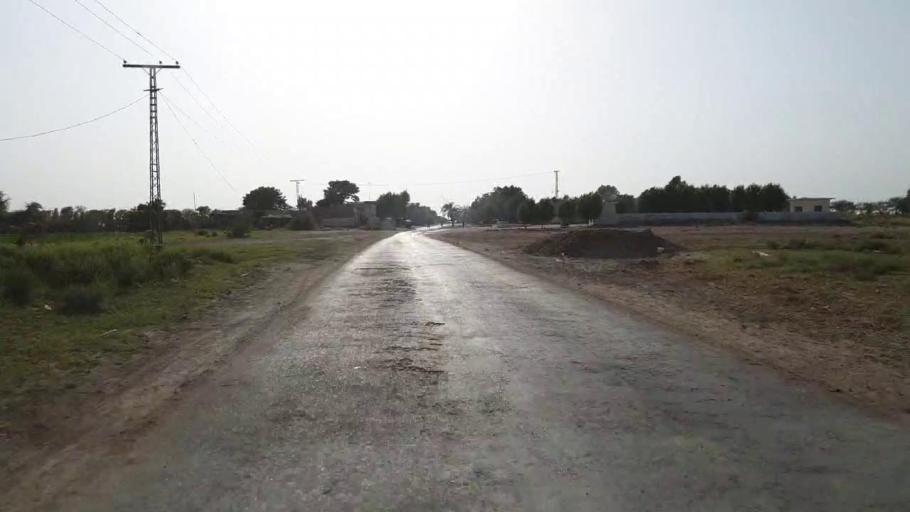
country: PK
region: Sindh
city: Jam Sahib
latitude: 26.3804
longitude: 68.8886
